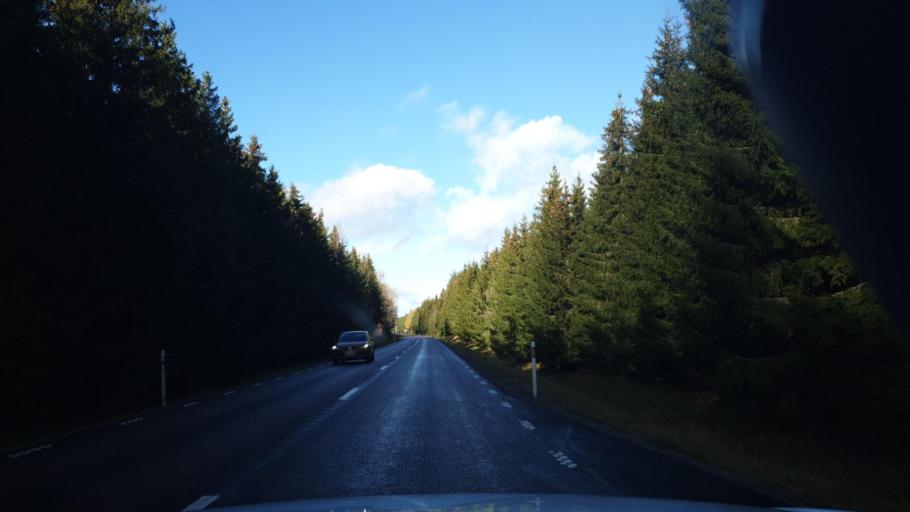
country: SE
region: Vaermland
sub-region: Arvika Kommun
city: Arvika
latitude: 59.5304
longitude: 12.7654
